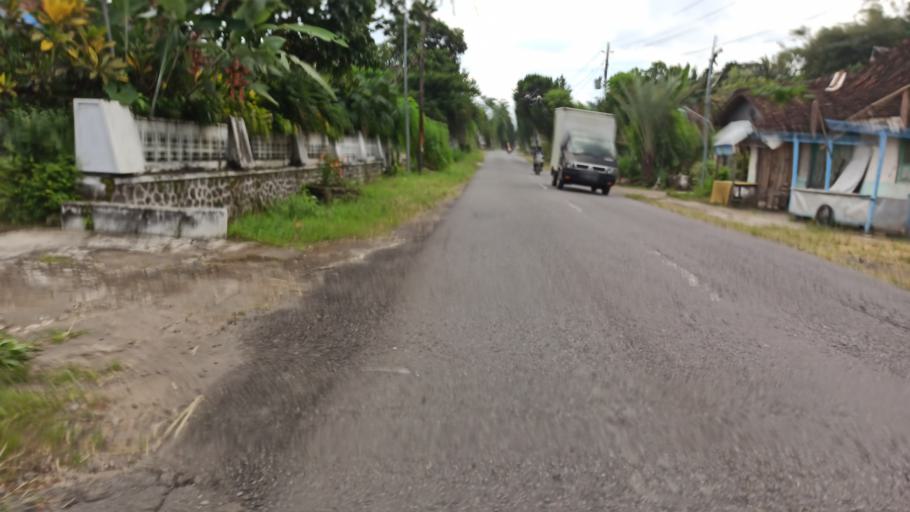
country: ID
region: Daerah Istimewa Yogyakarta
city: Sleman
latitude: -7.7003
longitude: 110.2899
